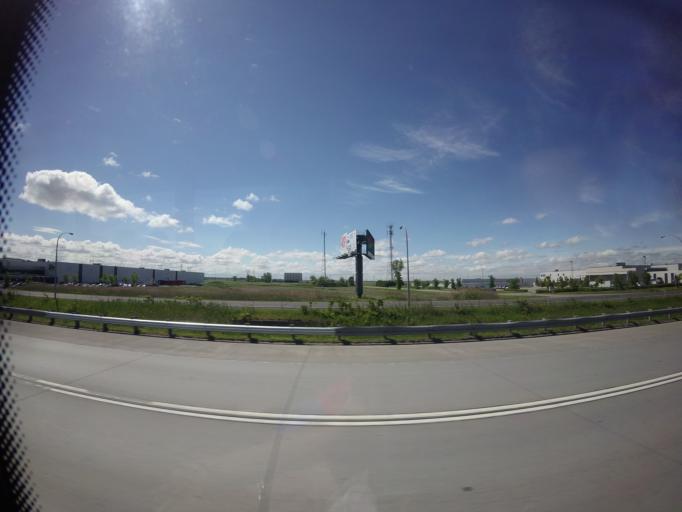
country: CA
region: Quebec
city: Saint-Bruno-de-Montarville
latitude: 45.5720
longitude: -73.3843
